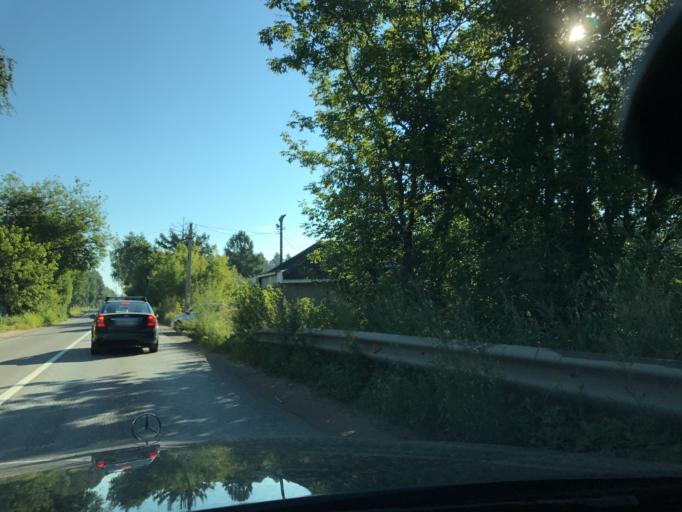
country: RU
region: Moskovskaya
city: Sverdlovskiy
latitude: 55.8590
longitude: 38.1371
